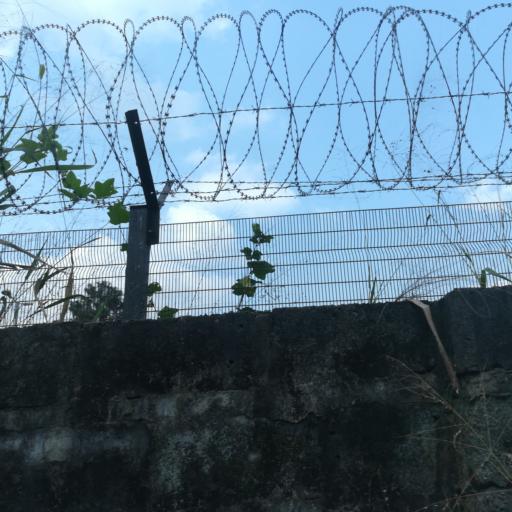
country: NG
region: Rivers
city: Okrika
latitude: 4.8175
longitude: 7.0986
